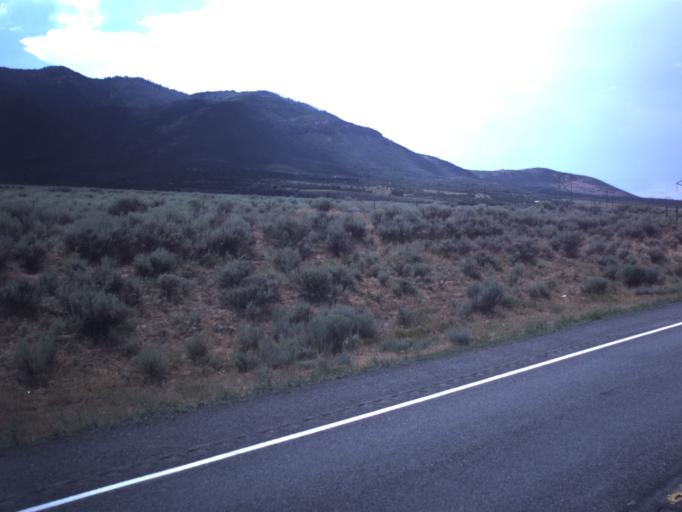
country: US
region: Utah
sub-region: Sanpete County
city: Fountain Green
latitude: 39.6902
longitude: -111.6848
